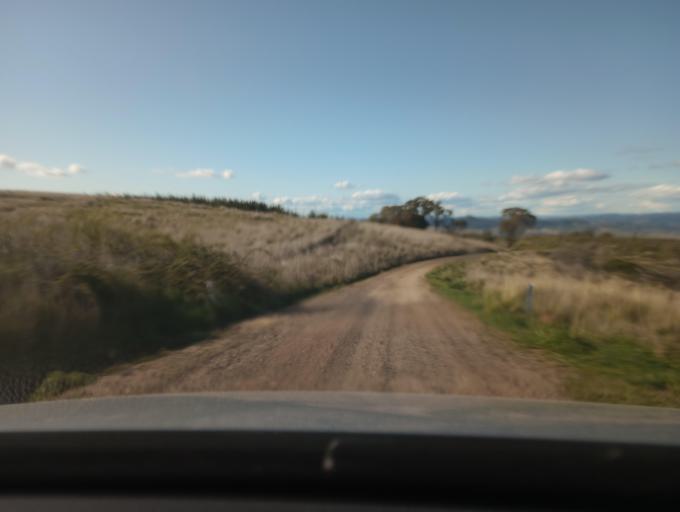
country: AU
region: New South Wales
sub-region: Blayney
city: Blayney
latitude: -33.4181
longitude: 149.3138
